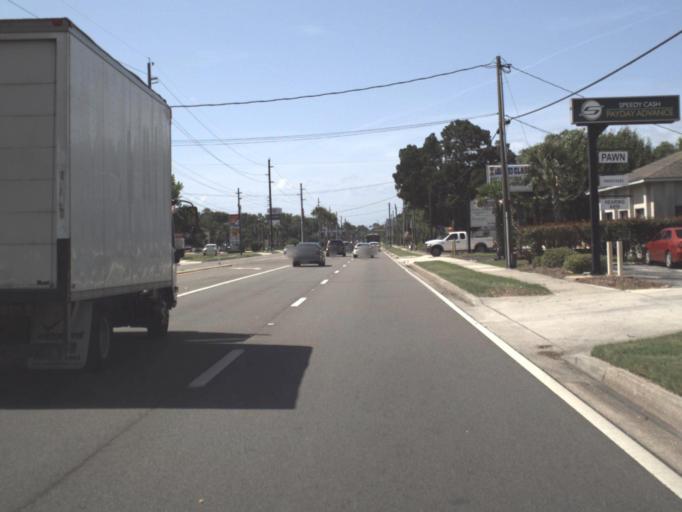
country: US
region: Florida
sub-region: Nassau County
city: Fernandina Beach
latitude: 30.6493
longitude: -81.4600
